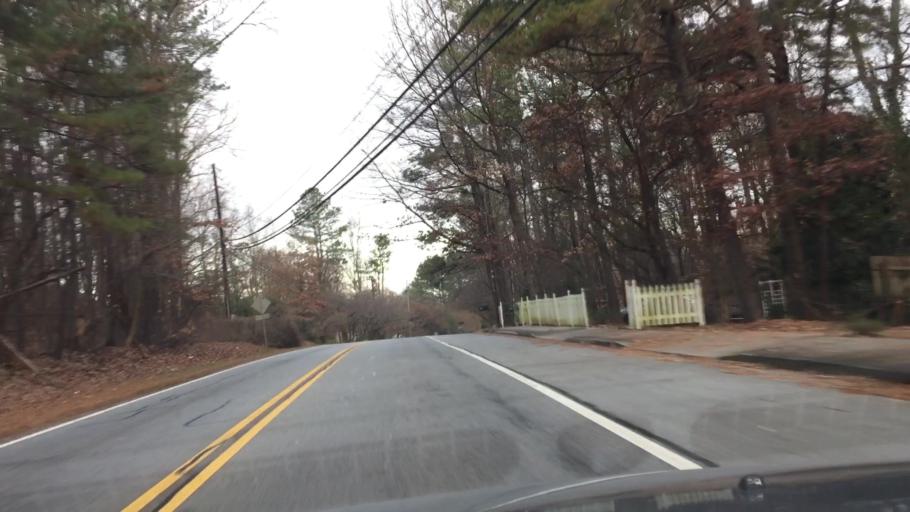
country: US
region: Georgia
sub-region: DeKalb County
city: Doraville
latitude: 33.9479
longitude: -84.2706
